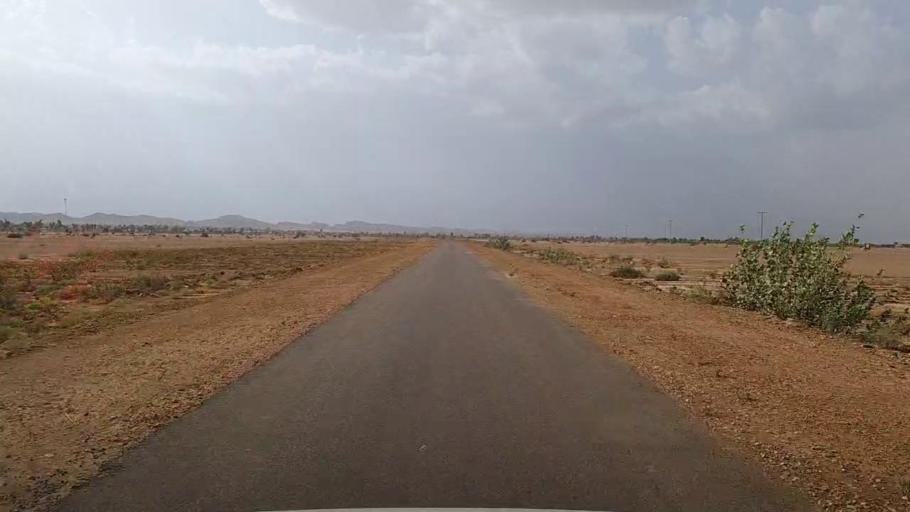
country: PK
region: Sindh
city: Jamshoro
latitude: 25.4738
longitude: 67.6744
